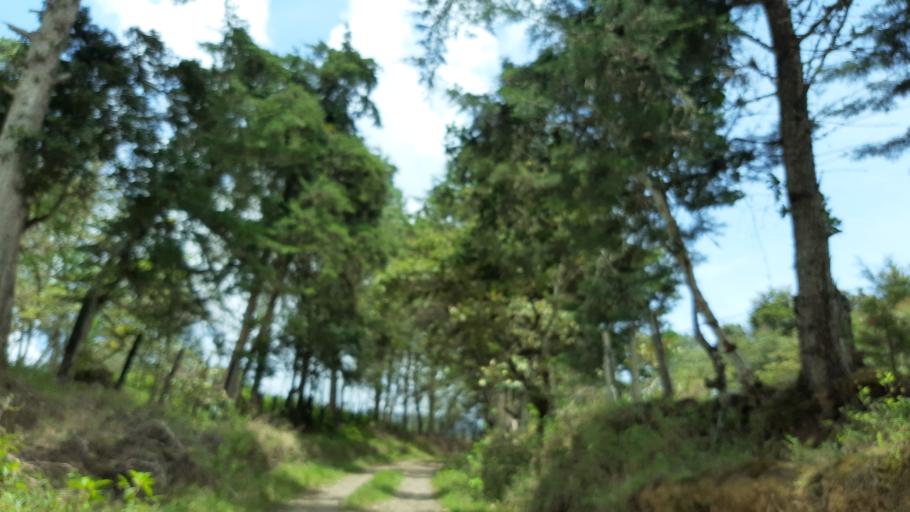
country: CO
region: Boyaca
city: Garagoa
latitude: 5.0625
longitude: -73.3589
